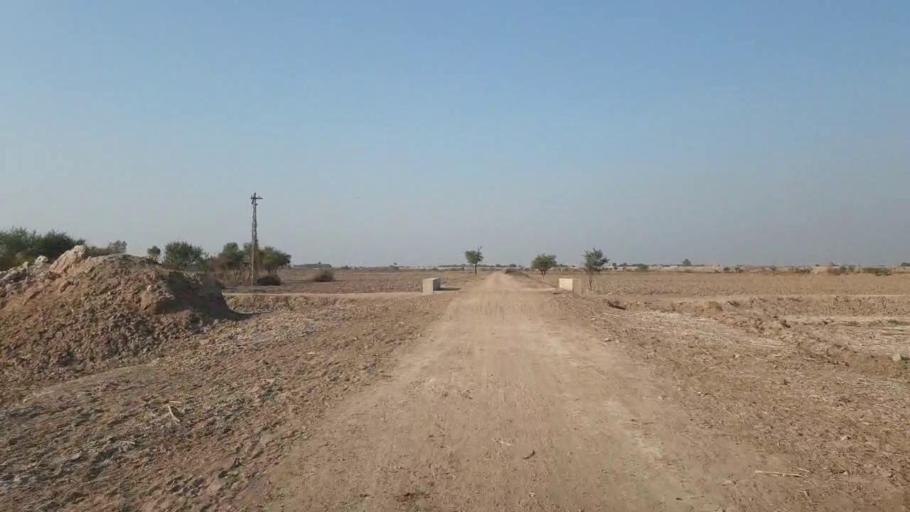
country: PK
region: Sindh
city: Mirpur Khas
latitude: 25.4530
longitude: 68.9333
